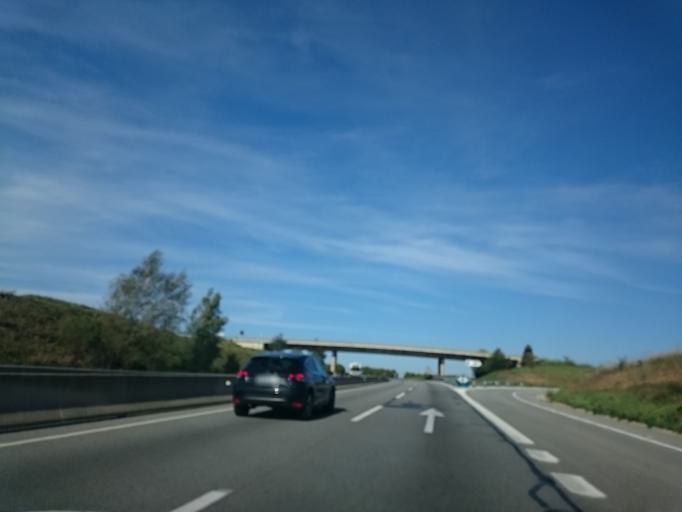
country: ES
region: Catalonia
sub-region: Provincia de Barcelona
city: Tona
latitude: 41.8257
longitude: 2.2338
